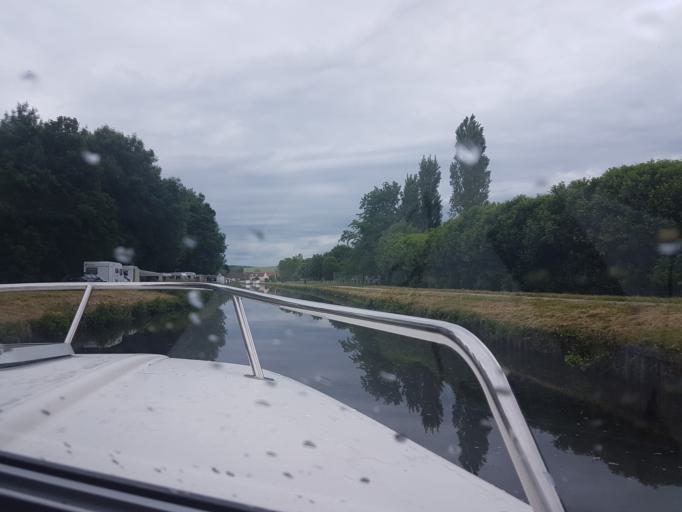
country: FR
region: Bourgogne
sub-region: Departement de l'Yonne
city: Saint-Bris-le-Vineux
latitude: 47.7059
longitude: 3.6363
